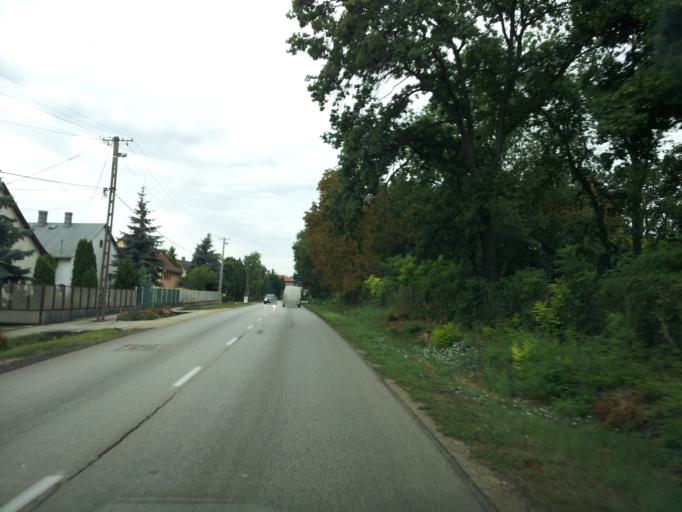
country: HU
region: Fejer
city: Velence
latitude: 47.2421
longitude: 18.6464
